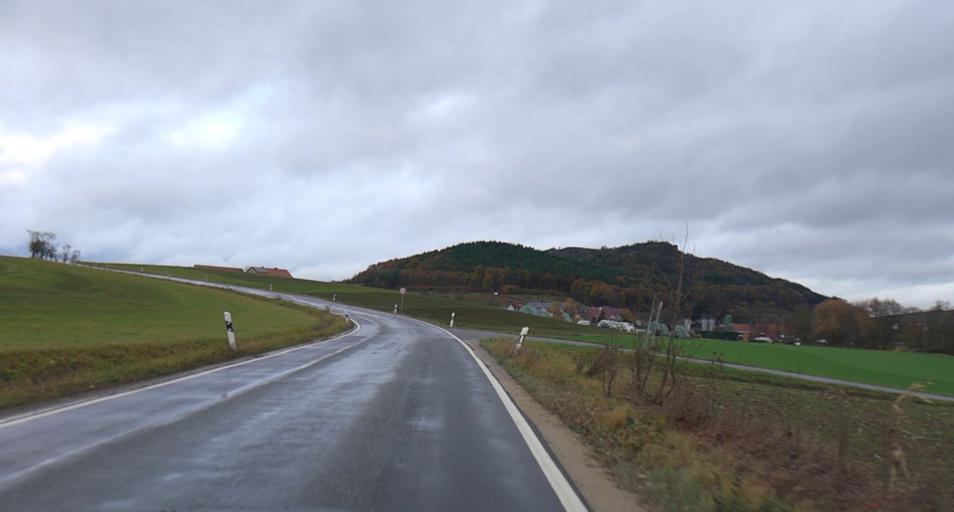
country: DE
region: Bavaria
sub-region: Upper Franconia
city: Leutenbach
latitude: 49.6956
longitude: 11.1652
